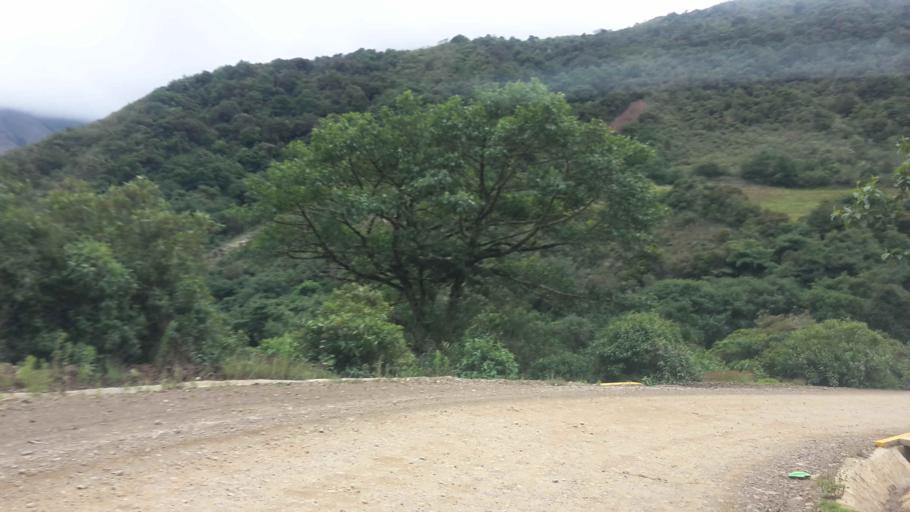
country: BO
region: Cochabamba
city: Totora
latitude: -17.5673
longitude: -65.2785
